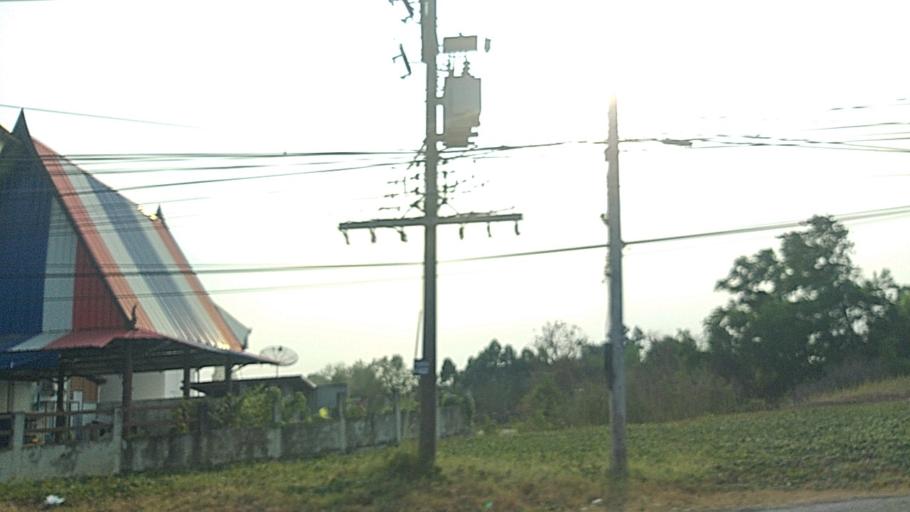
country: TH
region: Nakhon Nayok
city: Nakhon Nayok
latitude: 14.2041
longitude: 101.1887
